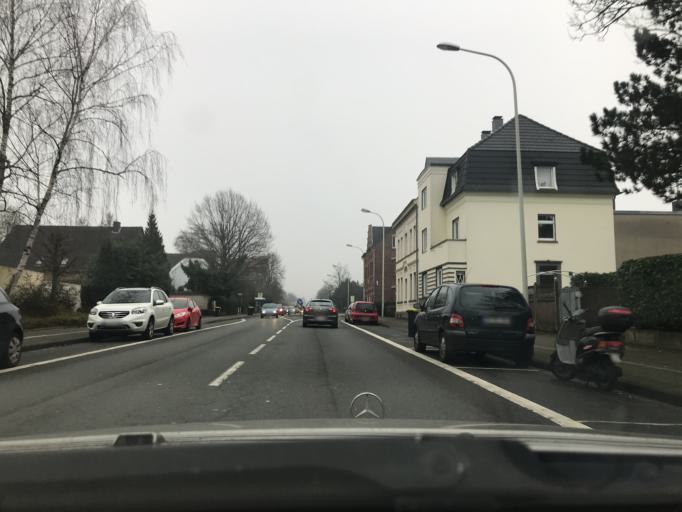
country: DE
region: North Rhine-Westphalia
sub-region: Regierungsbezirk Dusseldorf
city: Hilden
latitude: 51.1678
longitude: 6.9745
